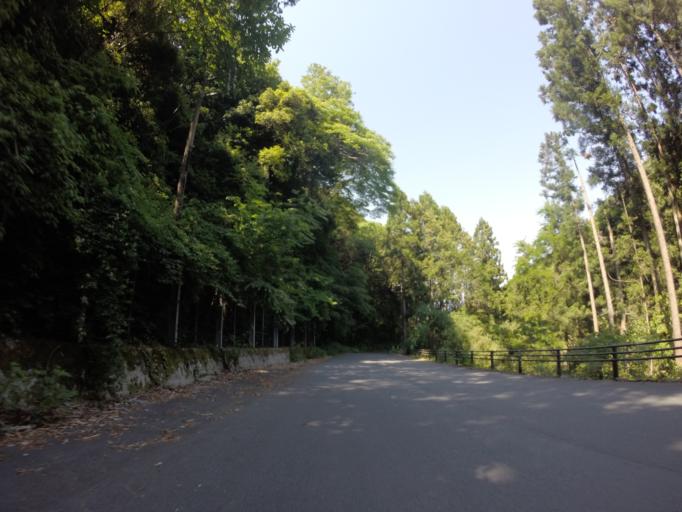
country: JP
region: Shizuoka
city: Fujinomiya
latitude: 35.1815
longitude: 138.5794
